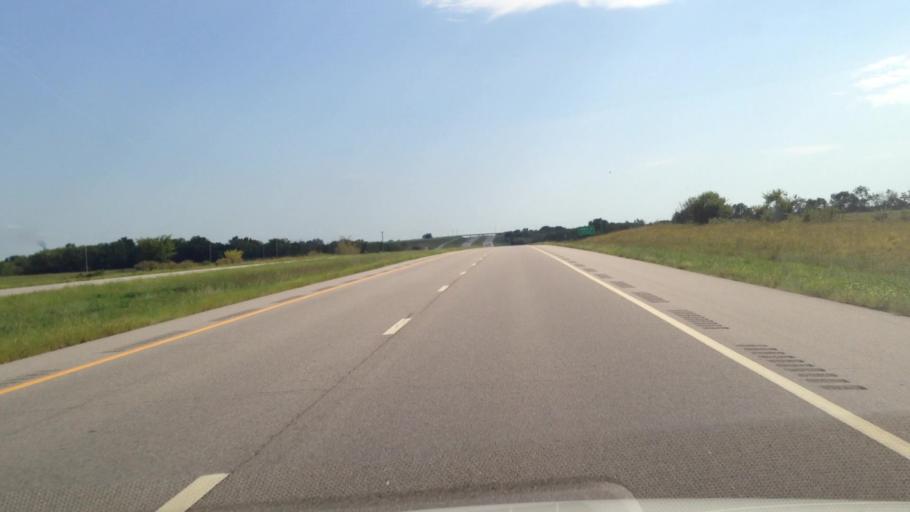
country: US
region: Kansas
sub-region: Linn County
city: La Cygne
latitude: 38.4219
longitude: -94.6876
